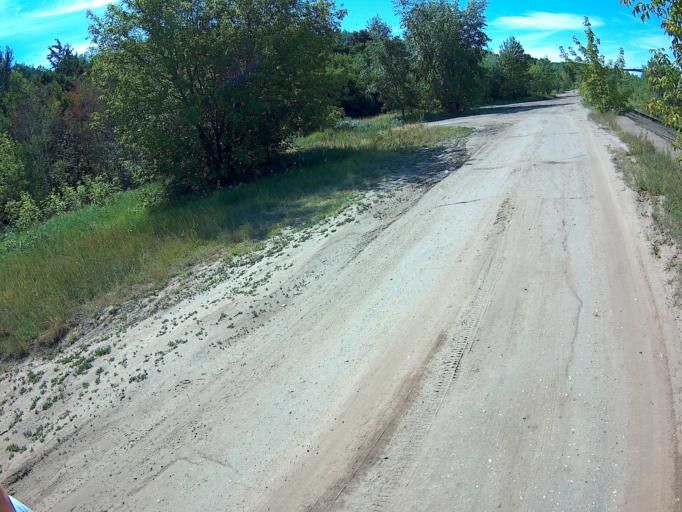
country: RU
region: Nizjnij Novgorod
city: Nizhniy Novgorod
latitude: 56.2575
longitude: 43.9644
